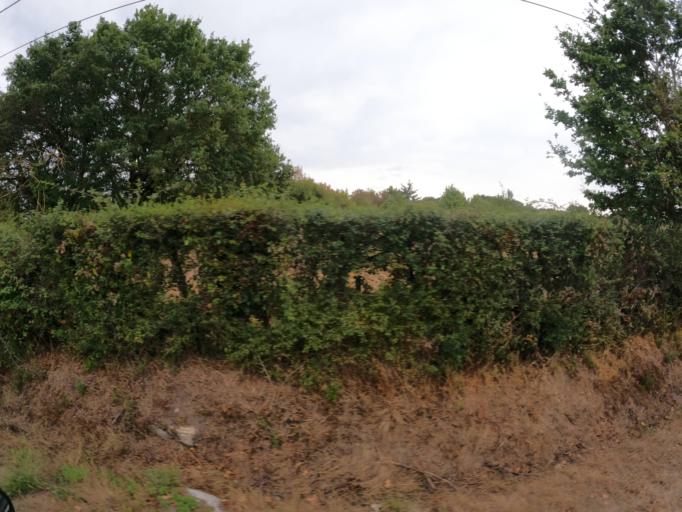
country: FR
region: Pays de la Loire
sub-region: Departement de la Vendee
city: Montaigu
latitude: 46.9719
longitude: -1.2857
